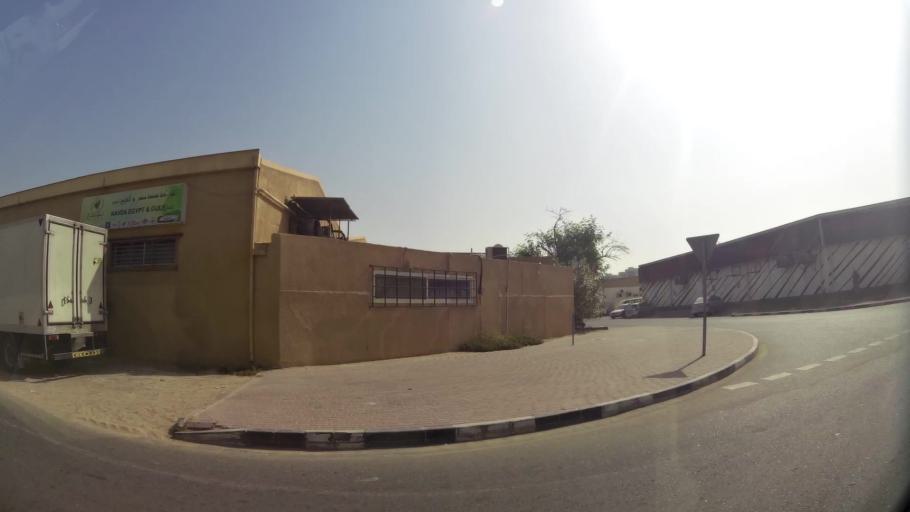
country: AE
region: Ash Shariqah
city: Sharjah
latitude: 25.2948
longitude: 55.3917
